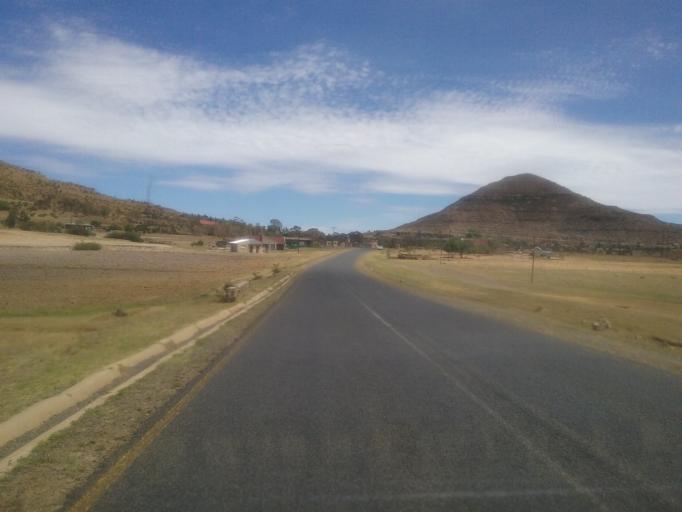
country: LS
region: Mafeteng
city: Mafeteng
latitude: -29.9591
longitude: 27.2913
